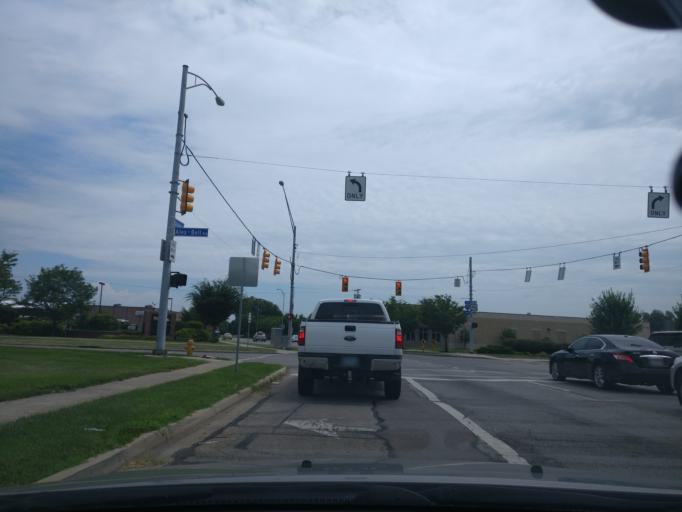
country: US
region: Ohio
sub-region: Montgomery County
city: West Carrollton City
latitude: 39.6760
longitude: -84.2406
